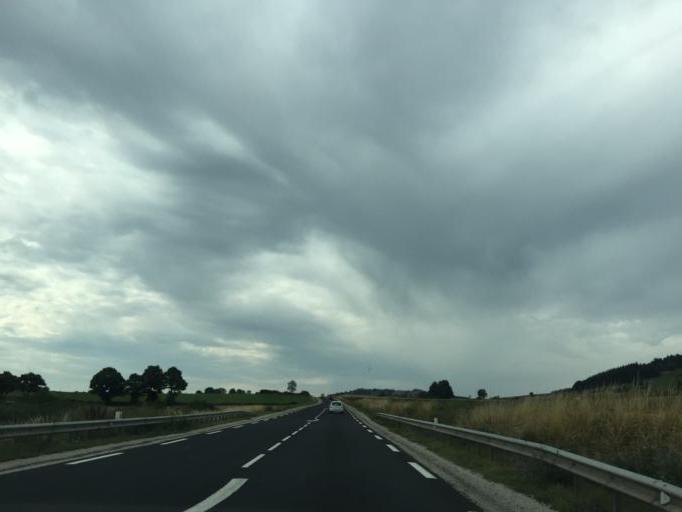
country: FR
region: Auvergne
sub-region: Departement de la Haute-Loire
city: Solignac-sur-Loire
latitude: 44.8879
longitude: 3.8477
